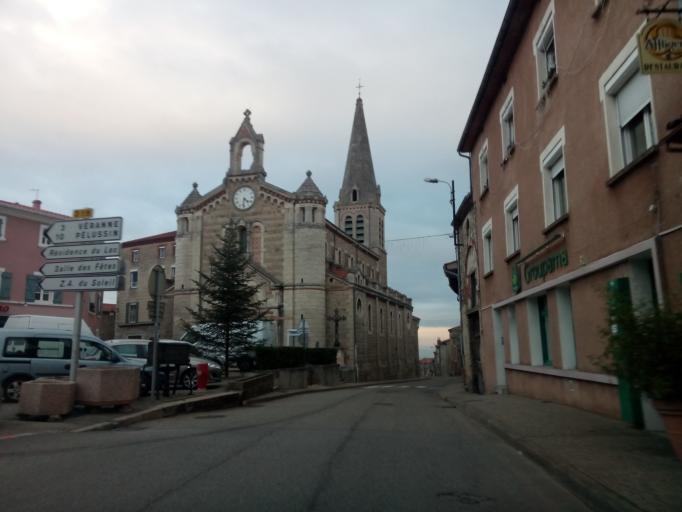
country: FR
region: Rhone-Alpes
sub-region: Departement de la Loire
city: Maclas
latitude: 45.3624
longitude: 4.6852
